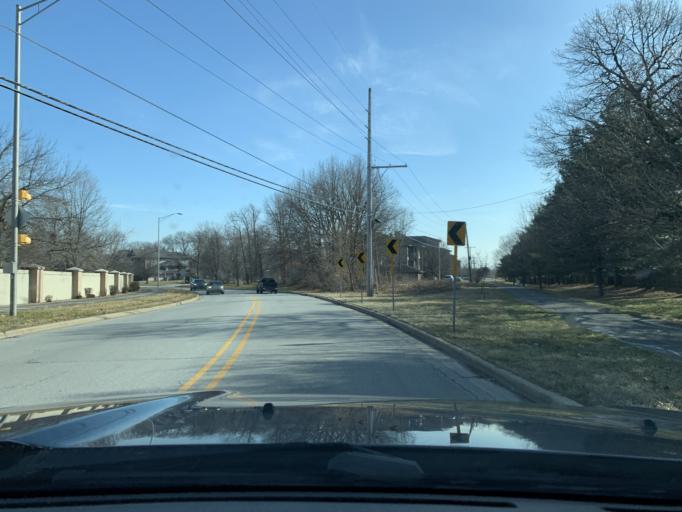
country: US
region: Indiana
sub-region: Lake County
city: Munster
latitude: 41.5265
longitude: -87.4904
